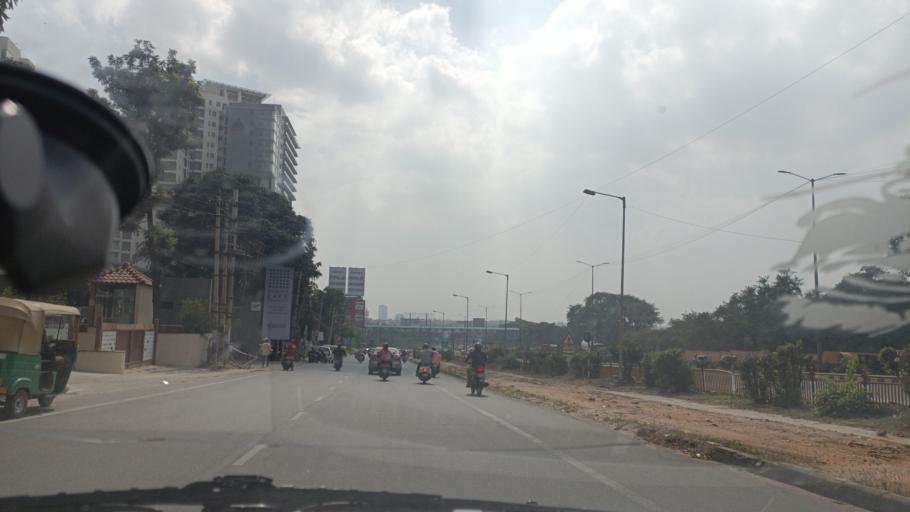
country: IN
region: Karnataka
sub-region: Bangalore Urban
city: Yelahanka
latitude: 13.0519
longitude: 77.5936
